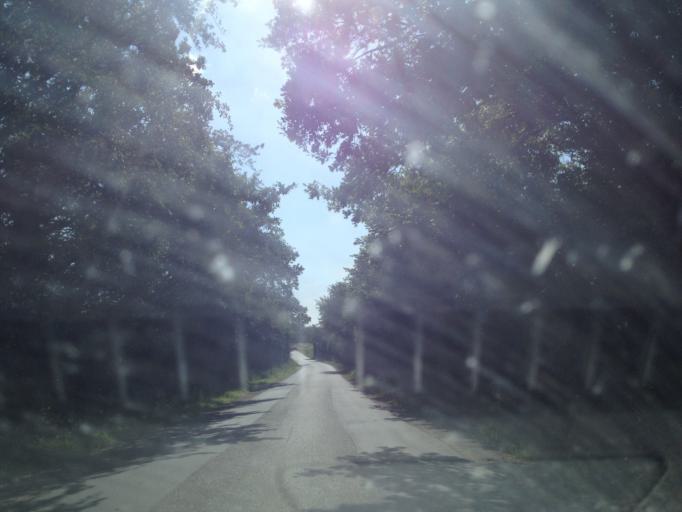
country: DK
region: South Denmark
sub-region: Kolding Kommune
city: Christiansfeld
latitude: 55.4013
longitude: 9.4911
